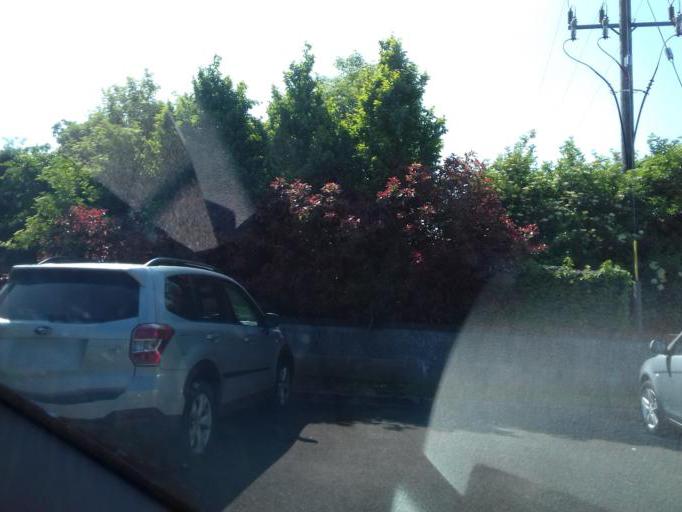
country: IE
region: Leinster
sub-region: An Mhi
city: Slane
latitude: 53.7111
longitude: -6.5456
